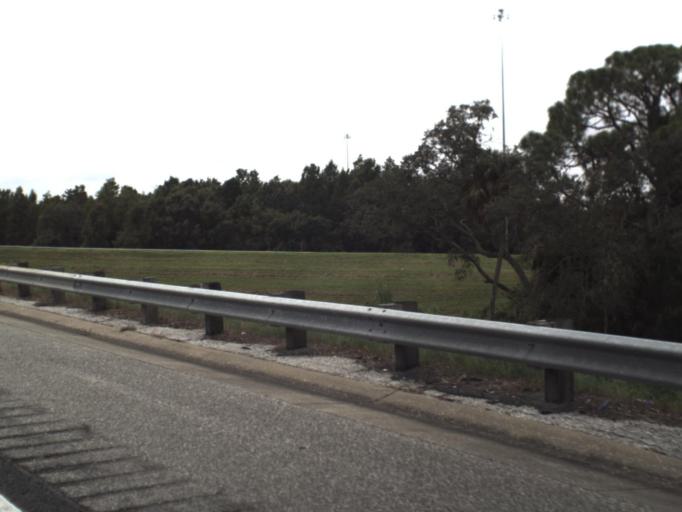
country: US
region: Florida
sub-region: Manatee County
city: Ellenton
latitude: 27.4935
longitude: -82.4735
